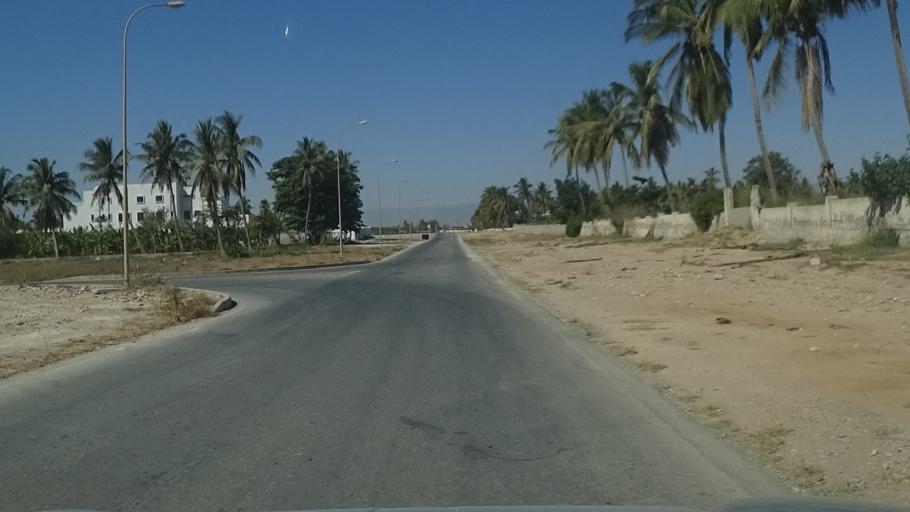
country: OM
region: Zufar
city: Salalah
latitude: 17.0343
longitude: 54.1562
